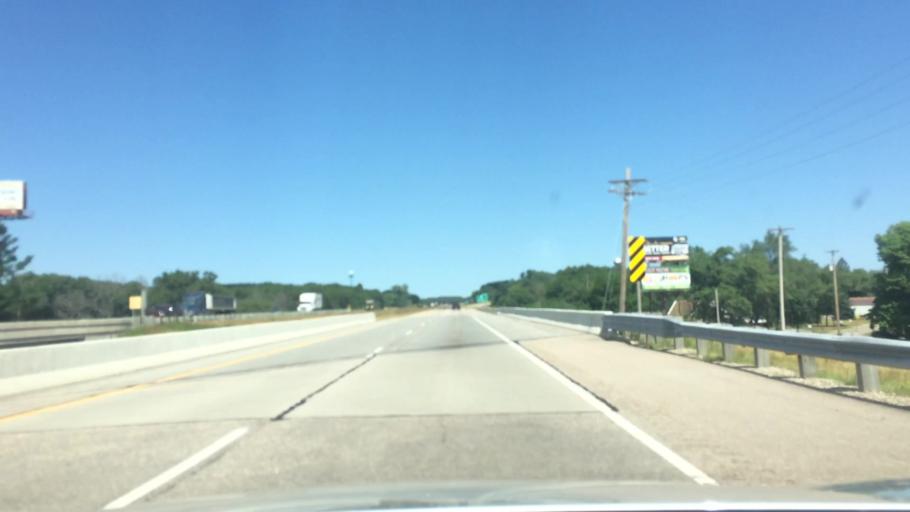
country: US
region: Wisconsin
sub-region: Marquette County
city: Westfield
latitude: 44.0276
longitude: -89.5216
